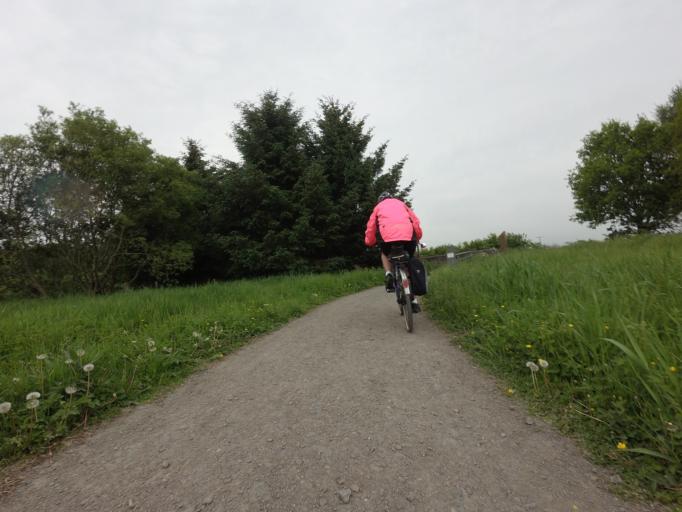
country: GB
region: Scotland
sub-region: Perth and Kinross
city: Milnathort
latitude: 56.2149
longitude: -3.4047
